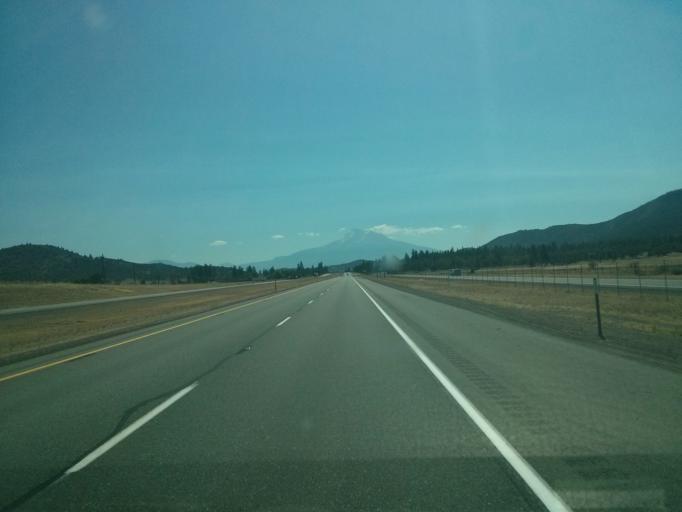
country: US
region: California
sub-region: Siskiyou County
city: Yreka
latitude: 41.6738
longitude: -122.6208
